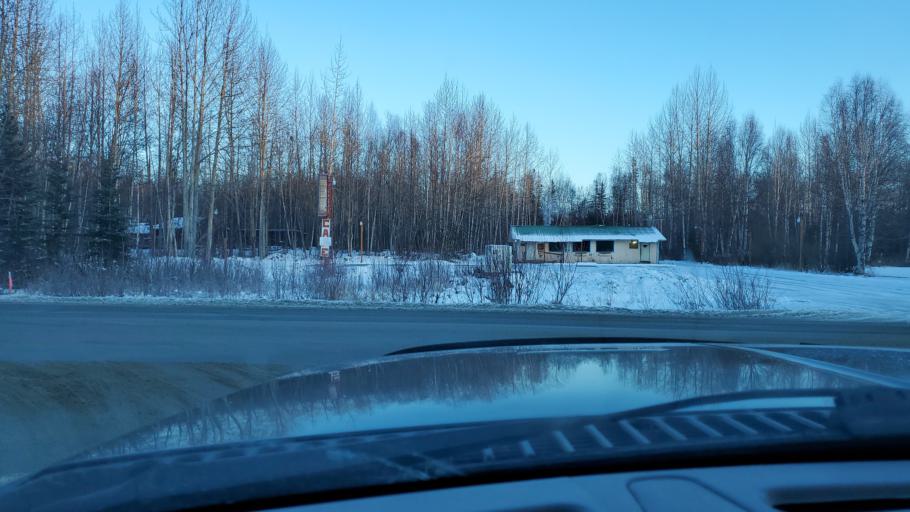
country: US
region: Alaska
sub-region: Matanuska-Susitna Borough
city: Fishhook
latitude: 61.6890
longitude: -149.2417
